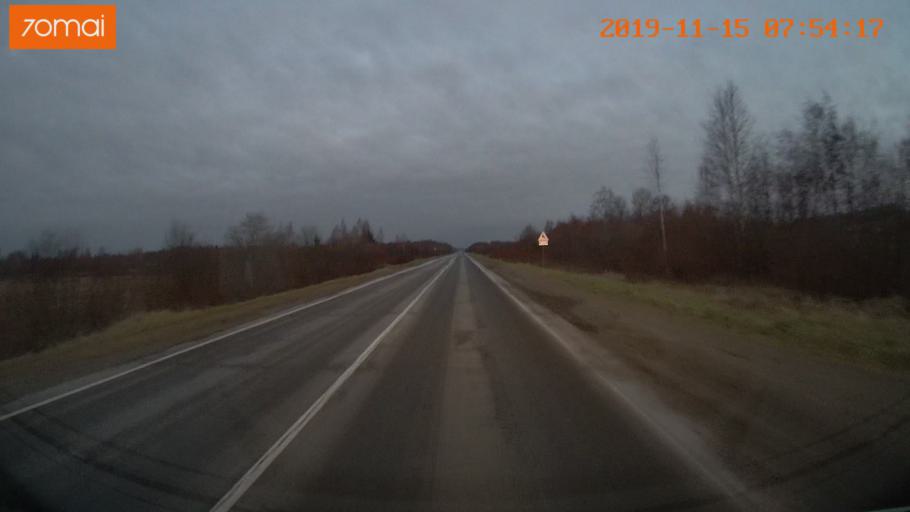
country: RU
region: Vologda
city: Cherepovets
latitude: 58.8970
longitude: 38.1777
